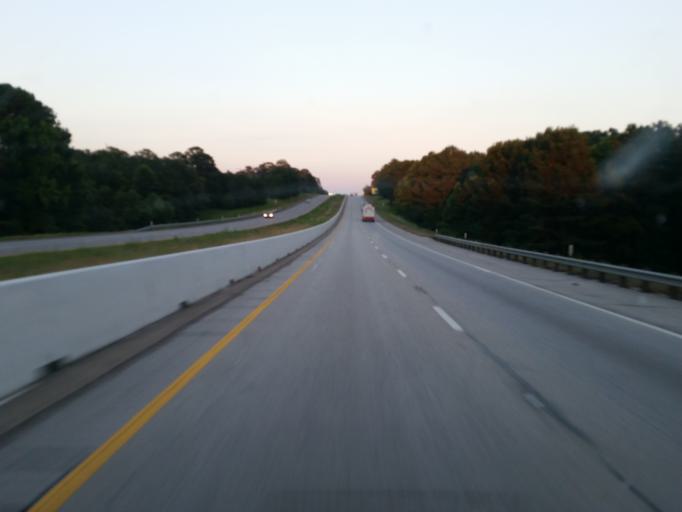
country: US
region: Texas
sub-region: Smith County
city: Hideaway
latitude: 32.4757
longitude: -95.4777
